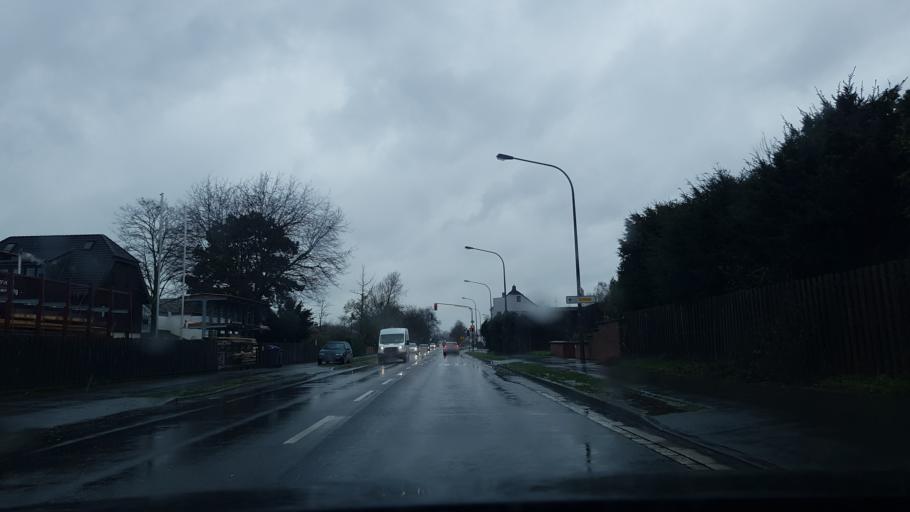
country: DE
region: North Rhine-Westphalia
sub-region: Regierungsbezirk Dusseldorf
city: Langenfeld
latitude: 51.1156
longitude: 6.9330
